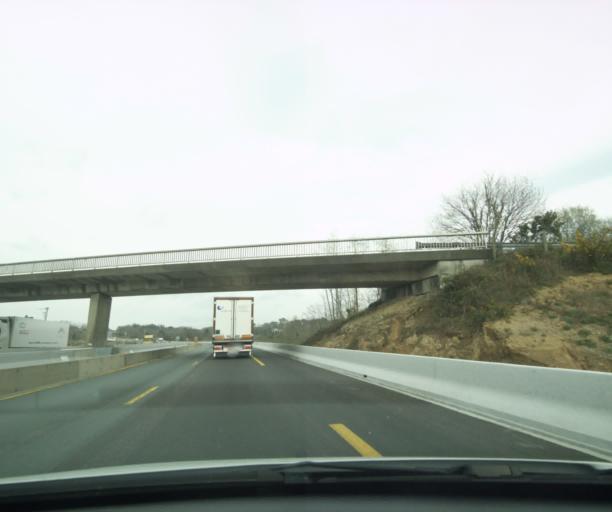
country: FR
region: Aquitaine
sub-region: Departement des Pyrenees-Atlantiques
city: Saint-Jean-de-Luz
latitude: 43.3770
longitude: -1.6473
